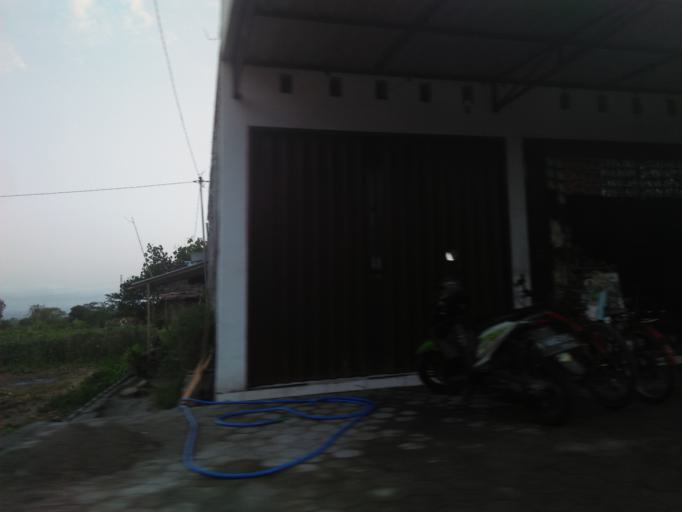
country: ID
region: Daerah Istimewa Yogyakarta
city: Sewon
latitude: -7.8447
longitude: 110.4003
